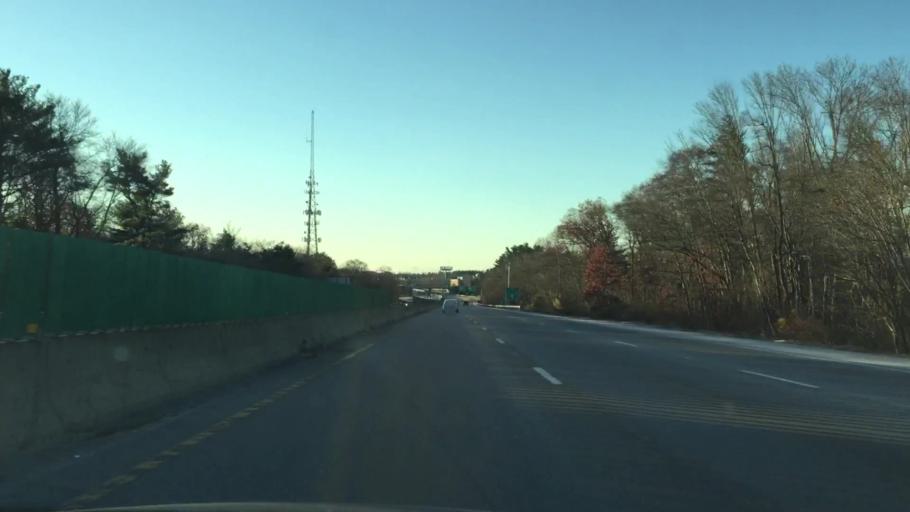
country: US
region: Massachusetts
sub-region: Plymouth County
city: Brockton
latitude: 42.0696
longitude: -71.0624
